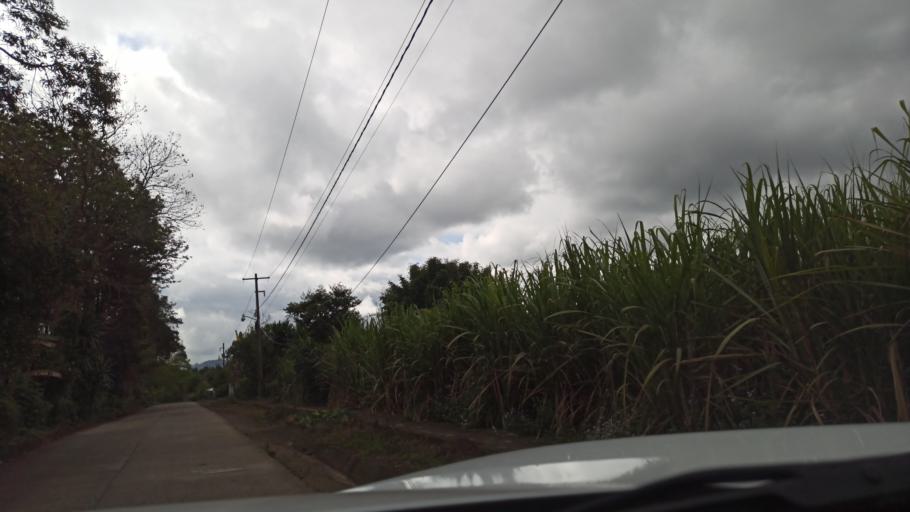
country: MX
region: Veracruz
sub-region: Chocaman
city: San Jose Neria
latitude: 19.0045
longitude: -97.0038
